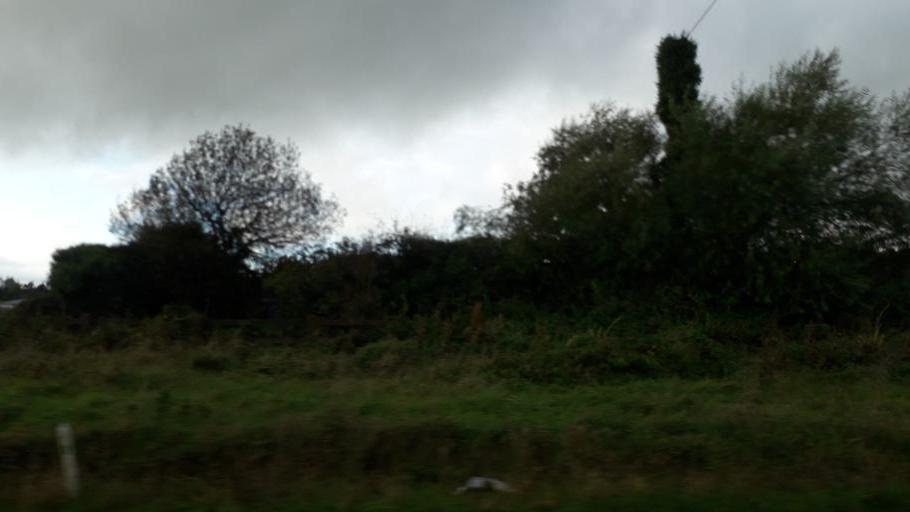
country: IE
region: Leinster
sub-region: An Longfort
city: Lanesborough
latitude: 53.7656
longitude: -8.0622
